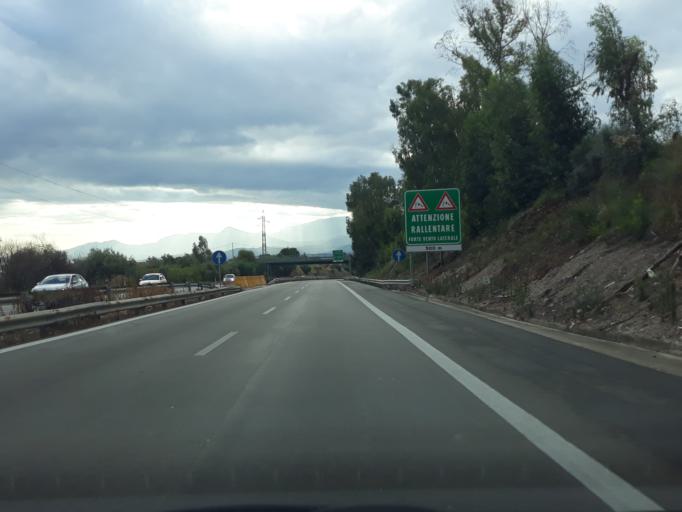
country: IT
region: Sicily
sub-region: Palermo
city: Termini Imerese
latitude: 37.9827
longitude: 13.6633
